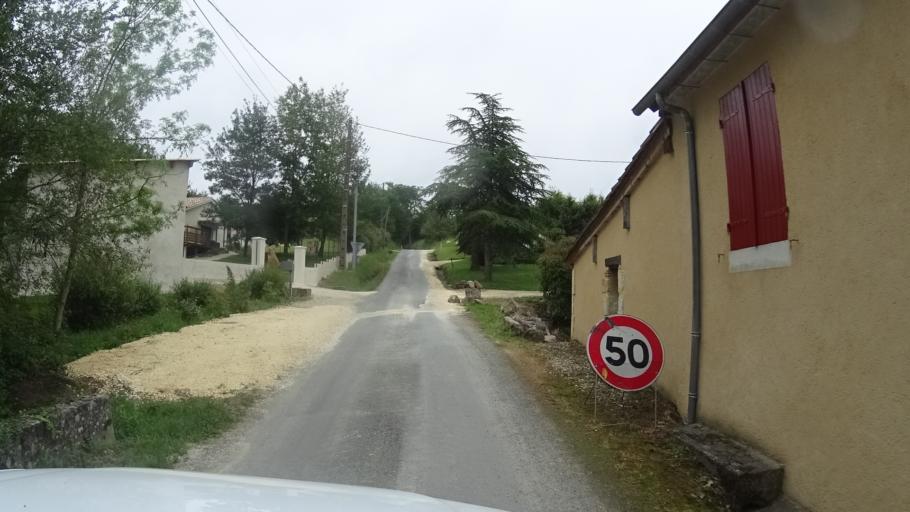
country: FR
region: Aquitaine
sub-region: Departement de la Dordogne
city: Bergerac
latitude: 44.9079
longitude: 0.4694
